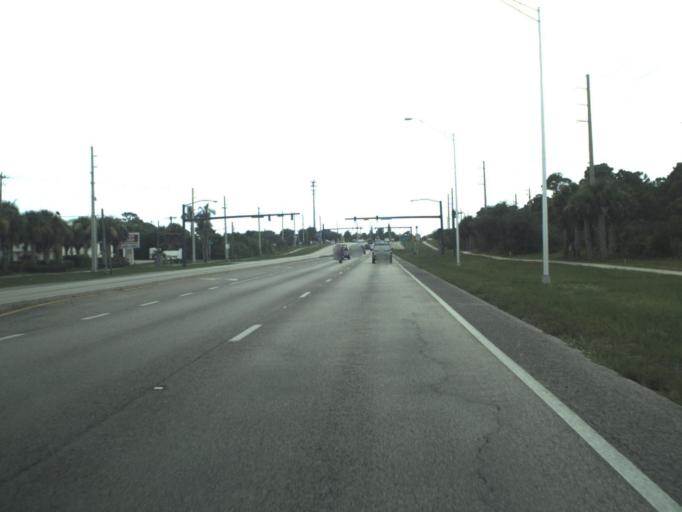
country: US
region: Florida
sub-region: Martin County
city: Hobe Sound
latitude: 27.1018
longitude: -80.1624
